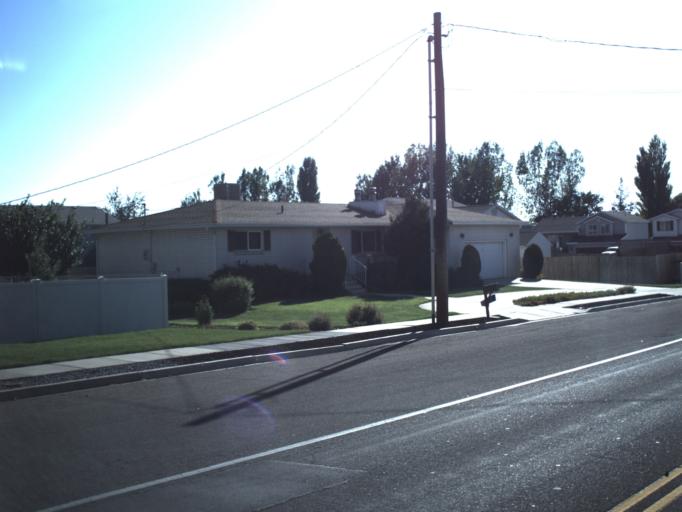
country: US
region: Utah
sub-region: Davis County
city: Clinton
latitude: 41.1399
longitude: -112.0405
